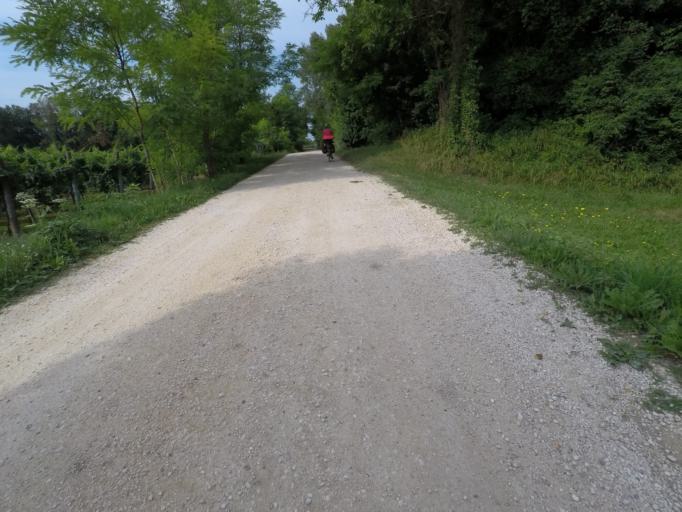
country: IT
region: Veneto
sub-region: Provincia di Treviso
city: Cappella Maggiore
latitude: 45.9702
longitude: 12.3365
